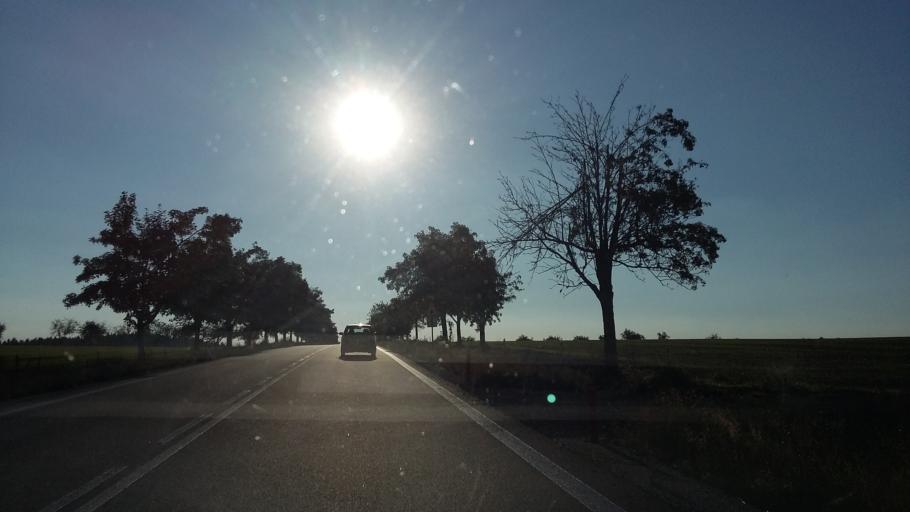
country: CZ
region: Vysocina
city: Kamenice
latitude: 49.3973
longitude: 15.7708
